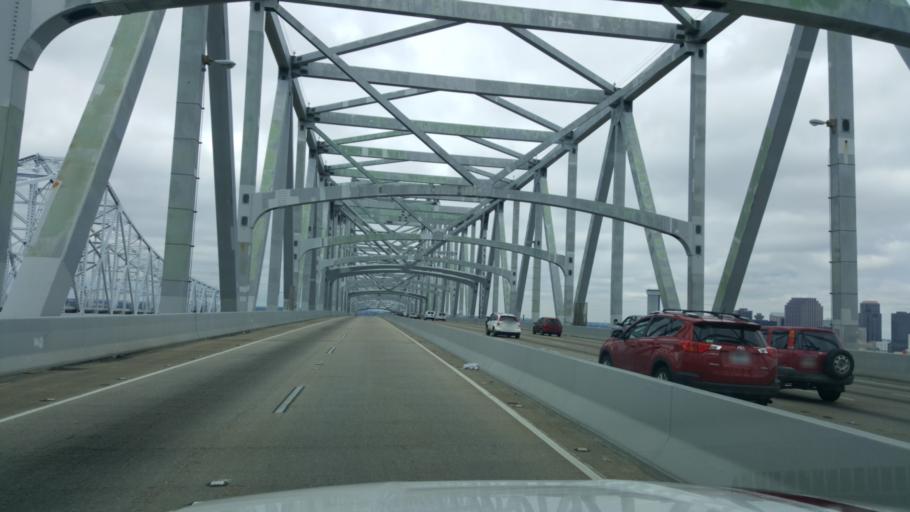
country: US
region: Louisiana
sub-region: Orleans Parish
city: New Orleans
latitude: 29.9398
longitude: -90.0568
